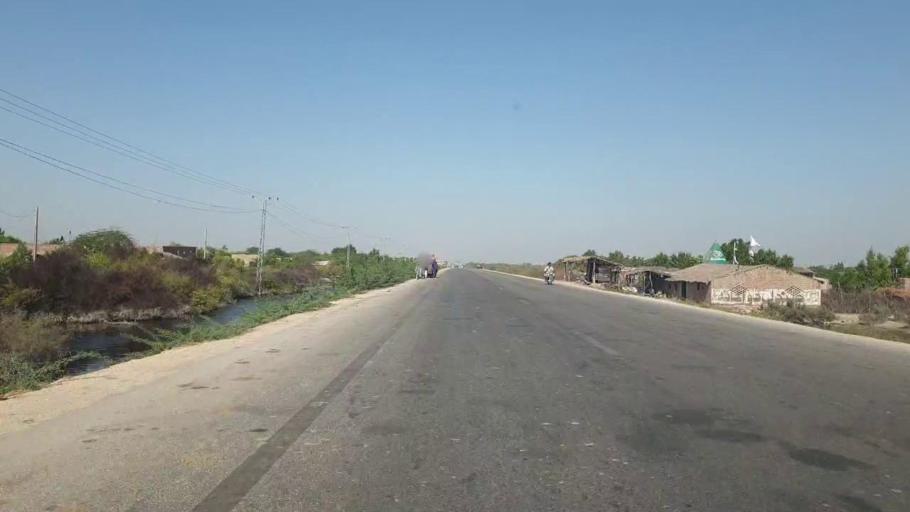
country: PK
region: Sindh
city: Talhar
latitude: 24.8536
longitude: 68.8165
